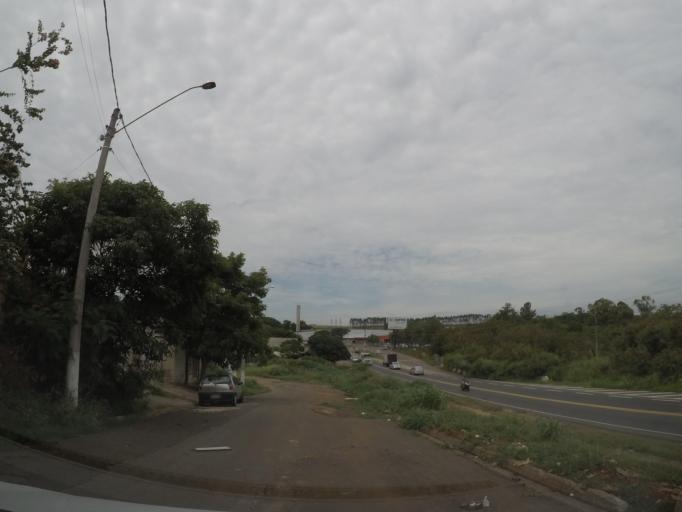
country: BR
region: Sao Paulo
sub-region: Hortolandia
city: Hortolandia
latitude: -22.8336
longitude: -47.2050
